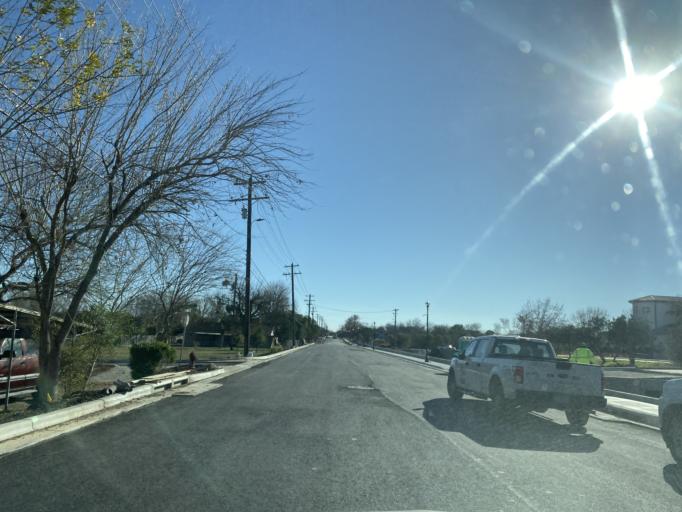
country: US
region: Texas
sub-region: Hays County
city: Kyle
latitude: 29.9963
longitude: -97.8758
